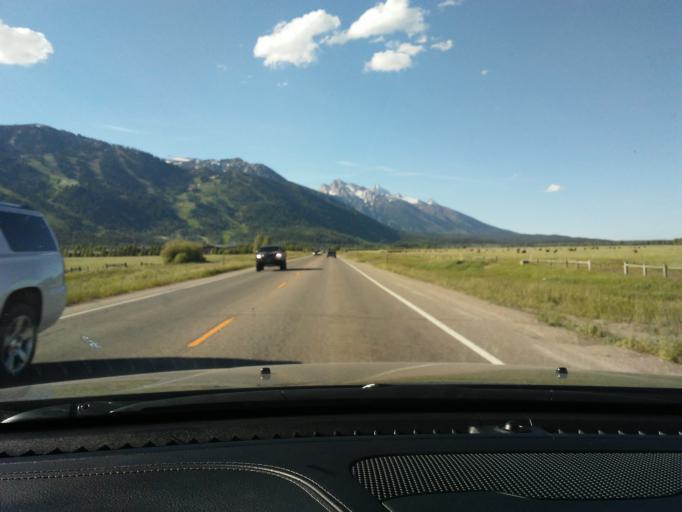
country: US
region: Wyoming
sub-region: Teton County
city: Moose Wilson Road
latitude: 43.5667
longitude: -110.8220
